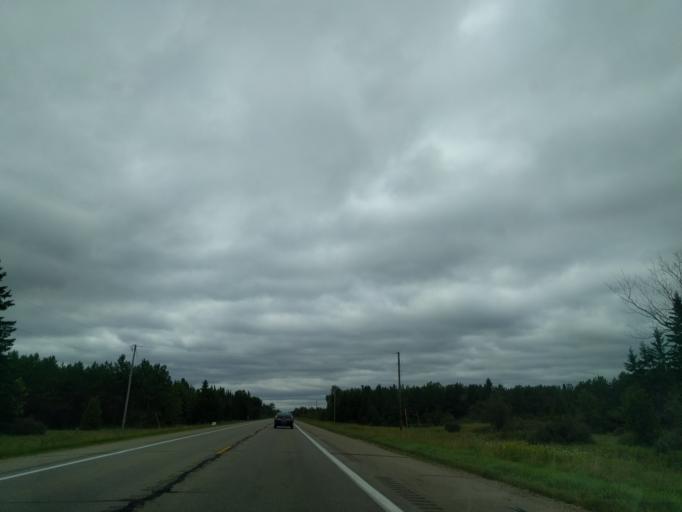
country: US
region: Michigan
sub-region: Delta County
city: Escanaba
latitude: 45.6232
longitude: -87.2099
